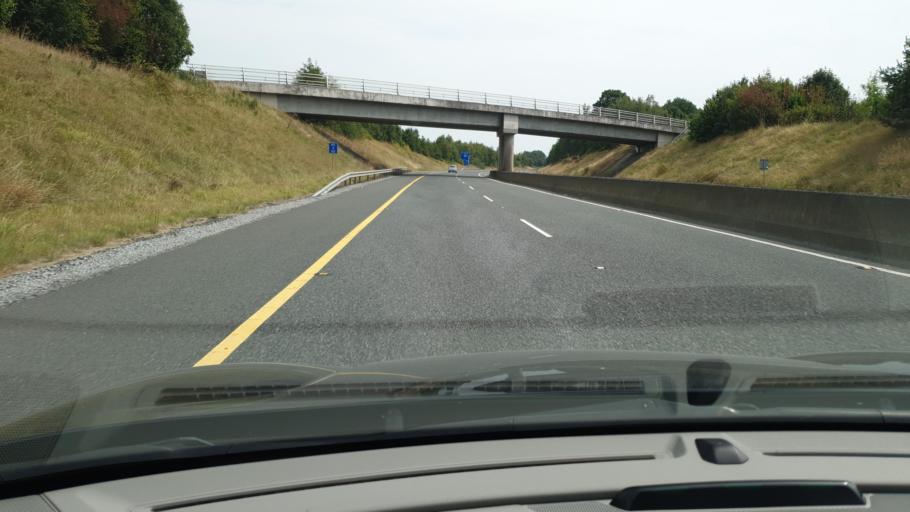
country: IE
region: Leinster
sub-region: An Mhi
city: Kells
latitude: 53.7138
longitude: -6.8743
